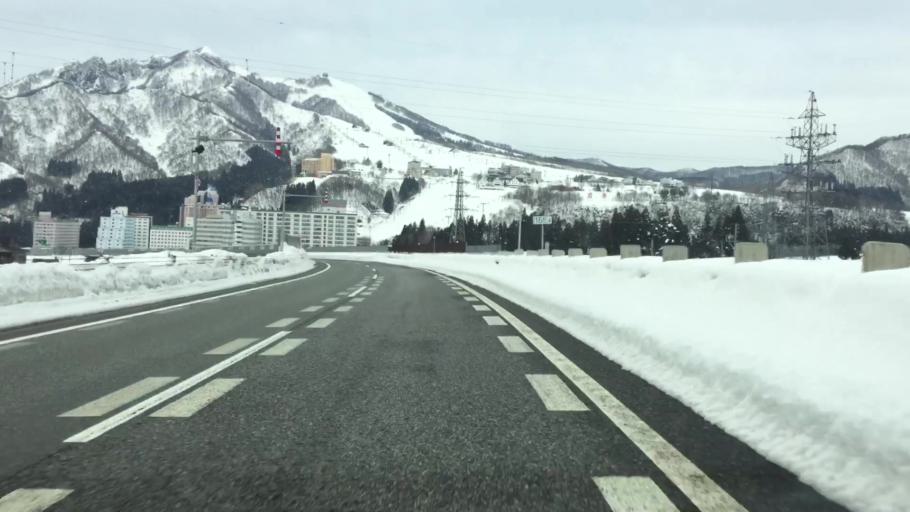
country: JP
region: Niigata
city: Shiozawa
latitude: 36.9235
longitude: 138.8415
